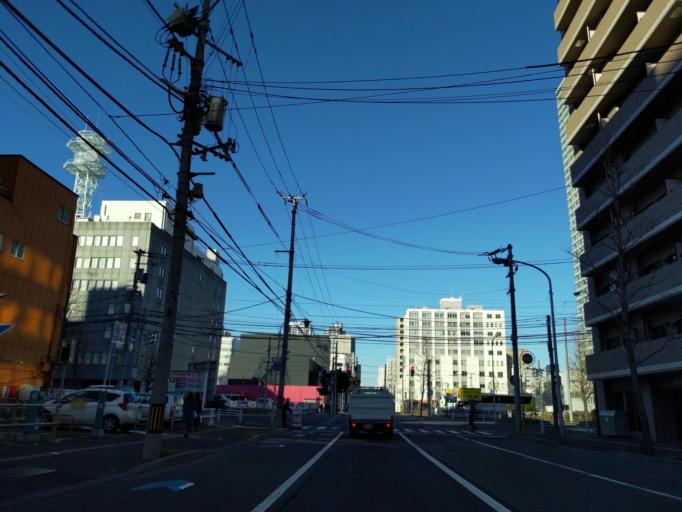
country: JP
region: Hokkaido
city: Sapporo
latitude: 43.0605
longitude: 141.3589
